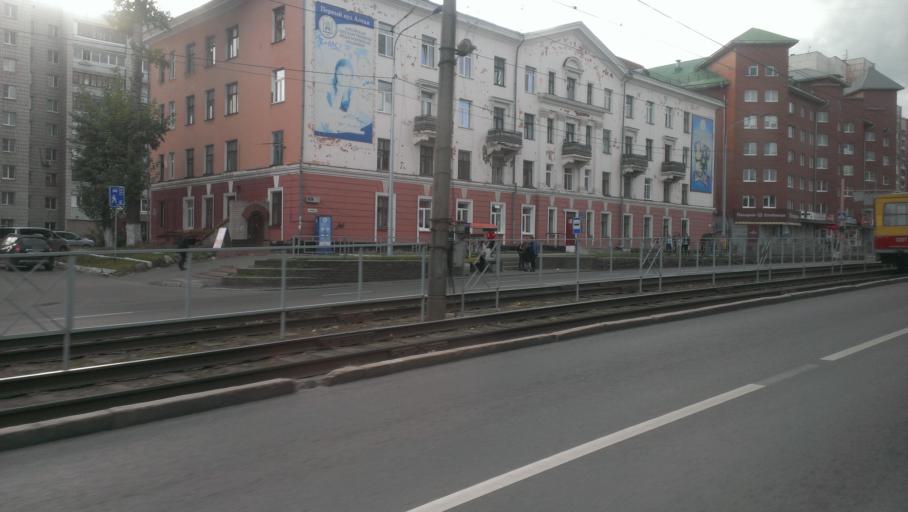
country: RU
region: Altai Krai
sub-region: Gorod Barnaulskiy
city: Barnaul
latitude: 53.3419
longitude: 83.7699
